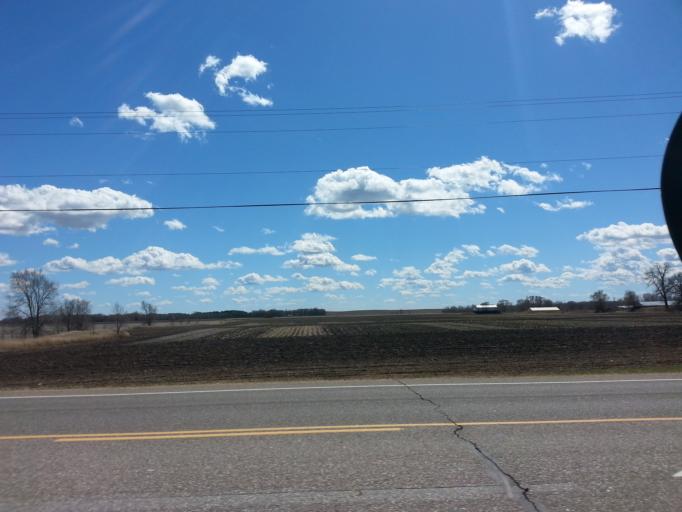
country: US
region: Minnesota
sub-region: Dakota County
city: Rosemount
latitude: 44.7174
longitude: -93.0939
